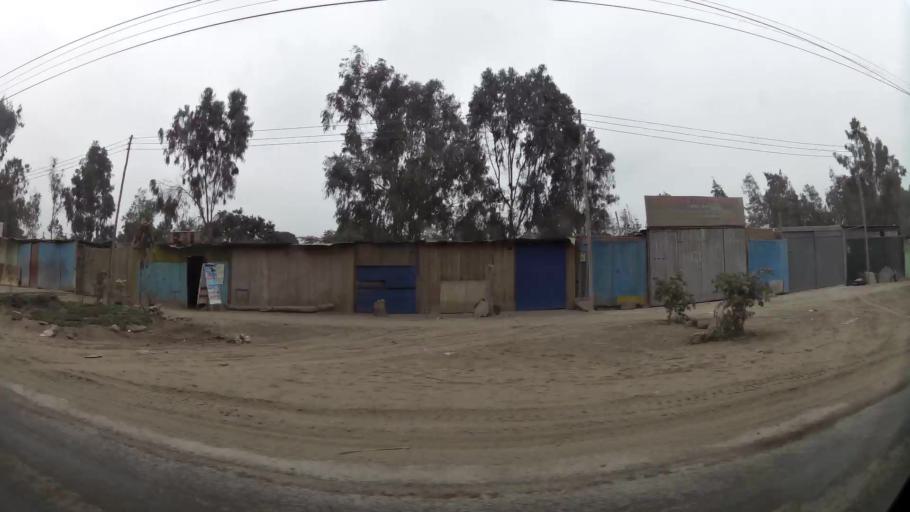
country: PE
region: Lima
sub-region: Lima
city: Surco
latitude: -12.1837
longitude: -76.9738
